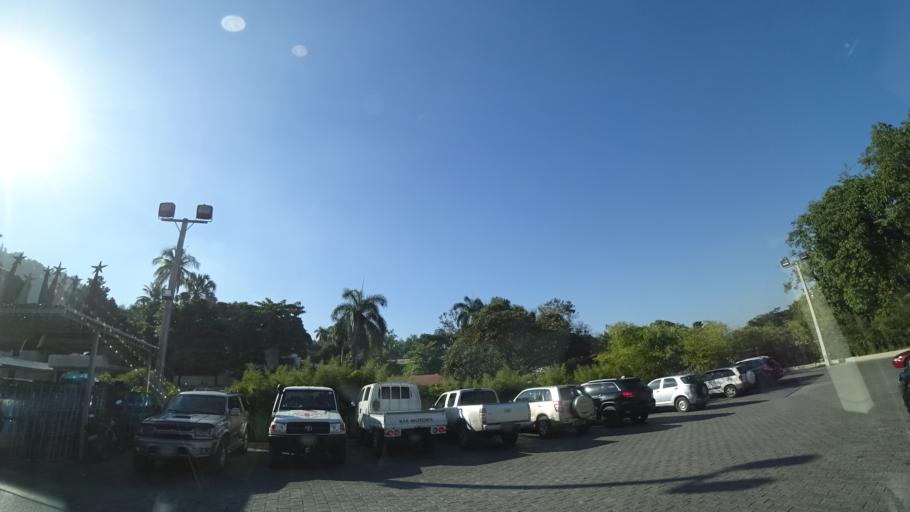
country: HT
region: Ouest
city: Petionville
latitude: 18.5079
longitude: -72.2842
